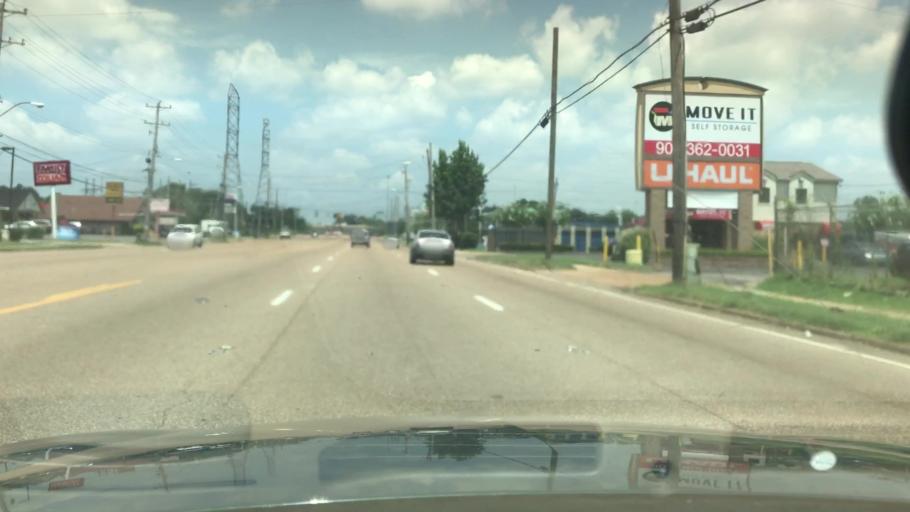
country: US
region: Mississippi
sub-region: De Soto County
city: Southaven
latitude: 35.0744
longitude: -89.9316
